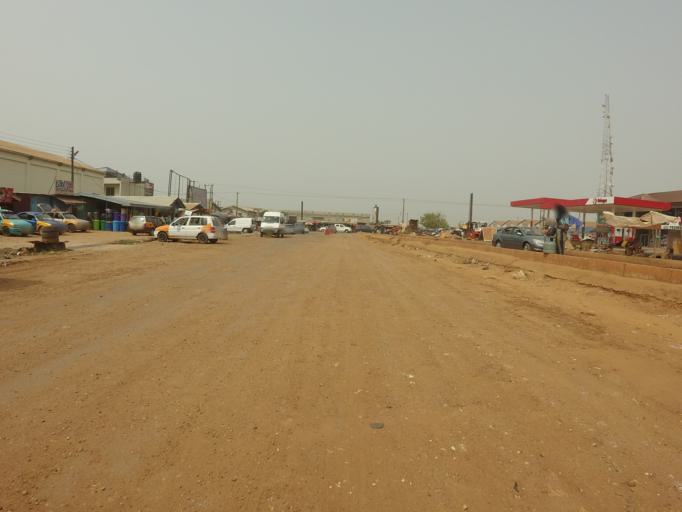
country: GH
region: Greater Accra
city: Medina Estates
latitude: 5.6369
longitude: -0.1264
